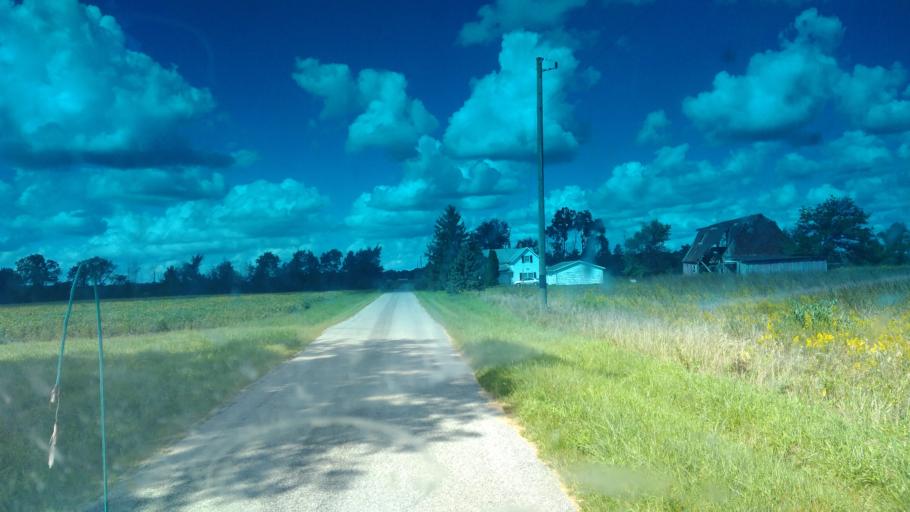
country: US
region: Ohio
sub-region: Hardin County
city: Kenton
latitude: 40.4876
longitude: -83.4996
